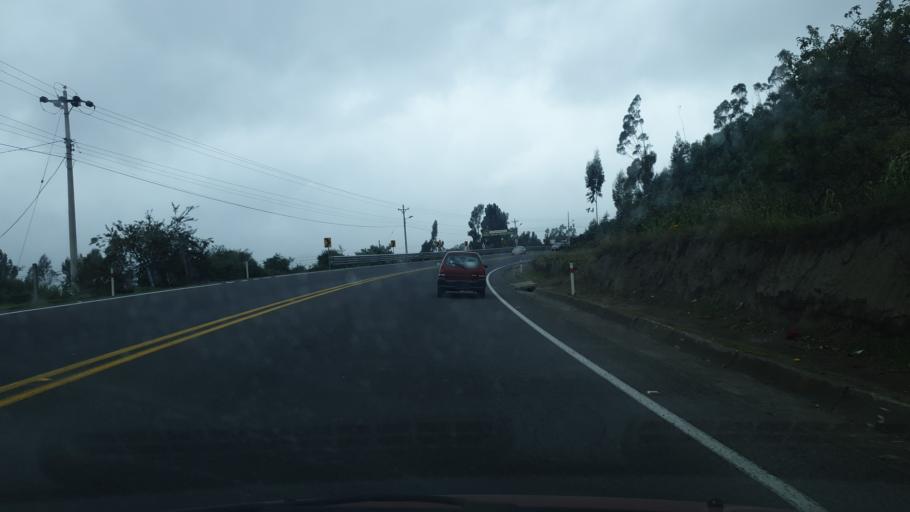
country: EC
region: Tungurahua
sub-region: Canton Quero
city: Quero
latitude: -1.3827
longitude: -78.6467
